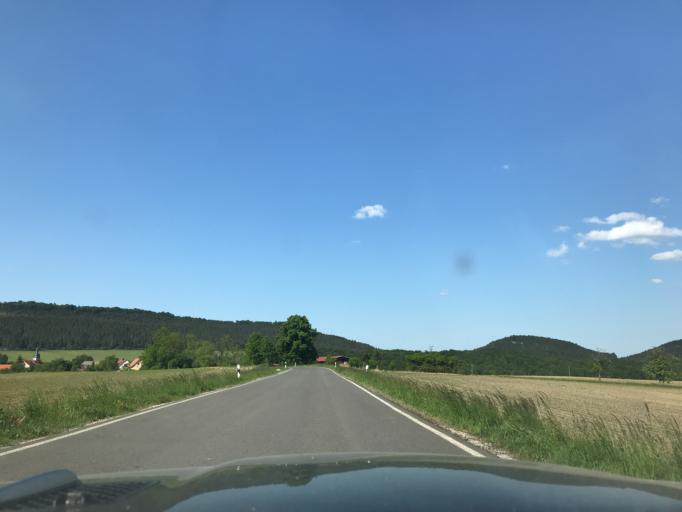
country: DE
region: Thuringia
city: Plaue
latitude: 50.7702
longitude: 10.9517
